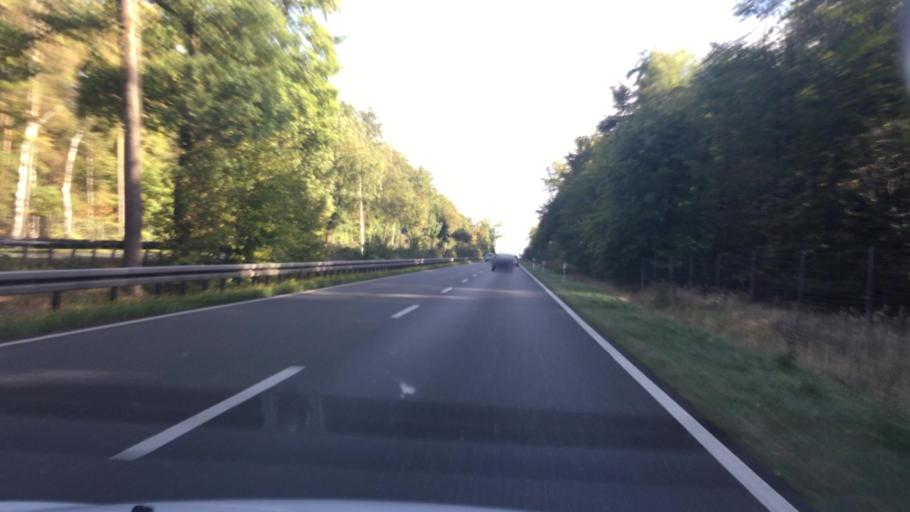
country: DE
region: Lower Saxony
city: Linsburg
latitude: 52.5684
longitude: 9.3162
